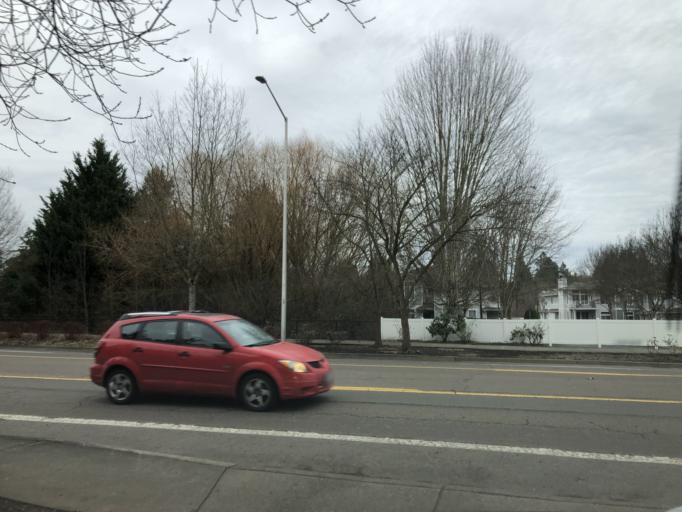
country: US
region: Oregon
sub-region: Washington County
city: Tigard
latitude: 45.4210
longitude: -122.7659
